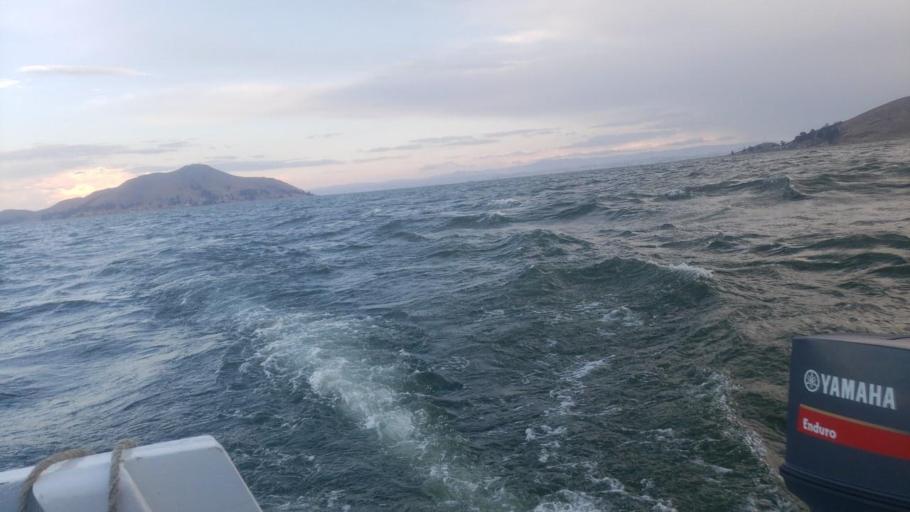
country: BO
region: La Paz
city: San Pedro
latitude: -16.2649
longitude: -68.8016
